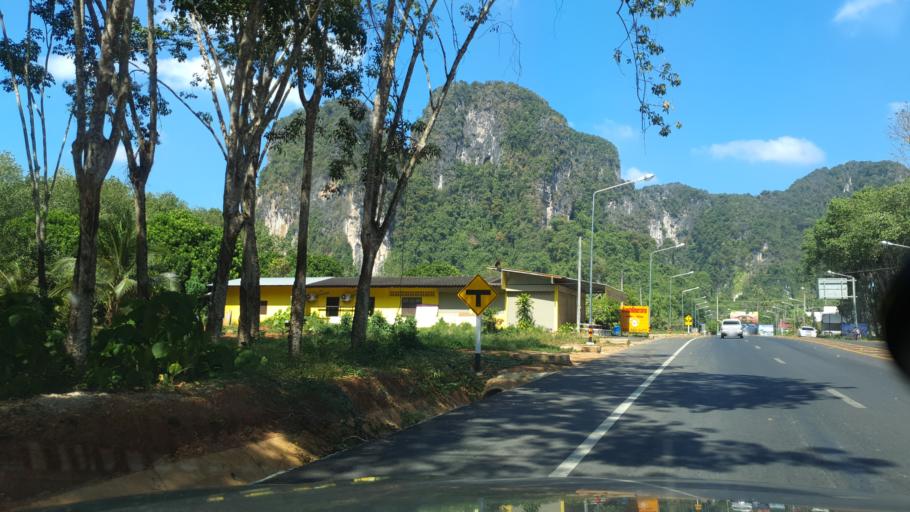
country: TH
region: Krabi
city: Krabi
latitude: 8.0771
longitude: 98.8573
